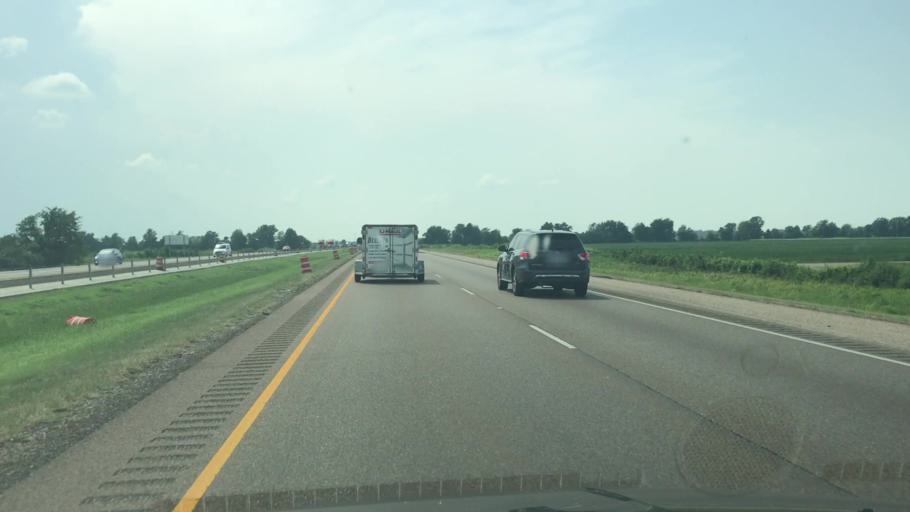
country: US
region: Arkansas
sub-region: Crittenden County
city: Earle
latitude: 35.1509
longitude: -90.3841
